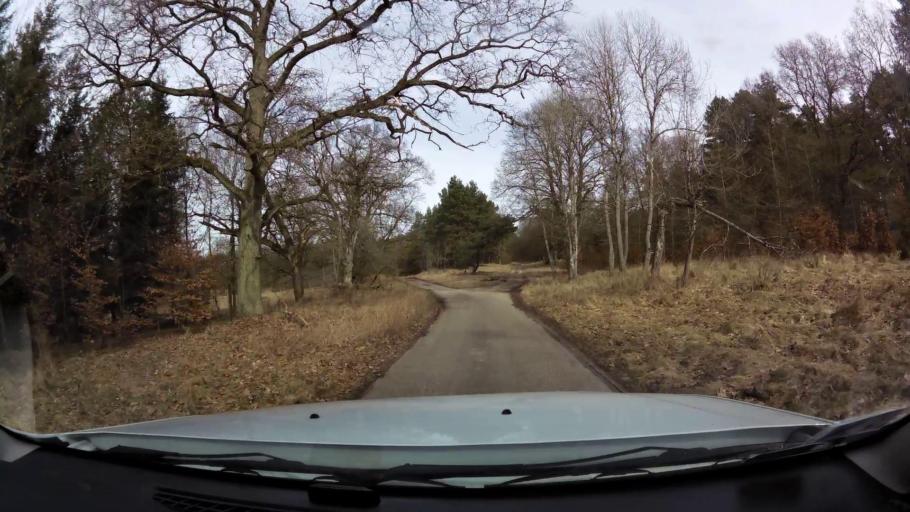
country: PL
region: West Pomeranian Voivodeship
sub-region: Powiat drawski
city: Drawsko Pomorskie
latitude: 53.4740
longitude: 15.6993
